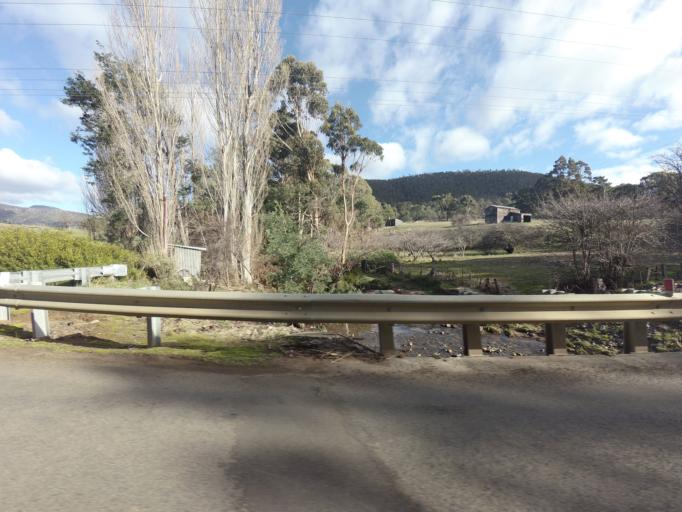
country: AU
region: Tasmania
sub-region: Derwent Valley
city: New Norfolk
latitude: -42.7930
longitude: 147.1223
